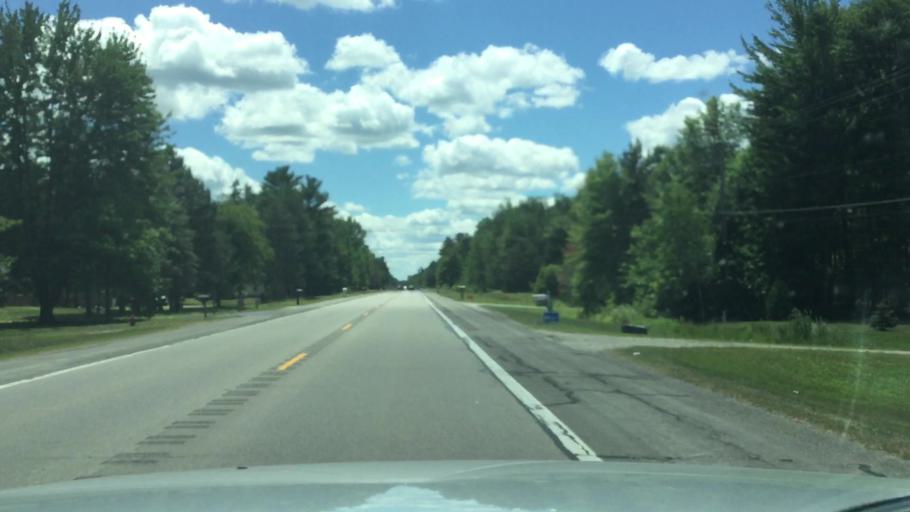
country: US
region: Michigan
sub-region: Saginaw County
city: Shields
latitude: 43.3934
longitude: -84.1312
